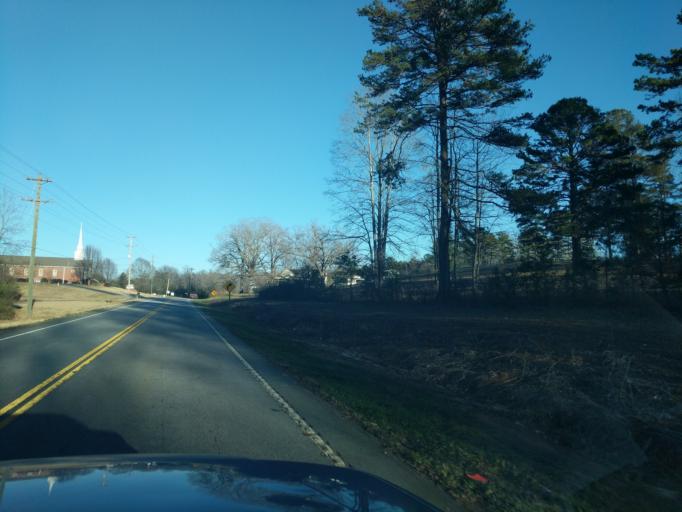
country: US
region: South Carolina
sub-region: Oconee County
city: Westminster
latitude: 34.6871
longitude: -83.1478
